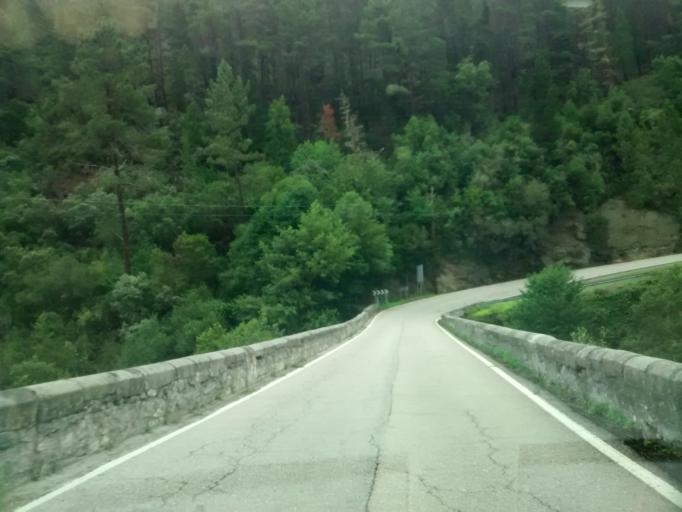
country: ES
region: Galicia
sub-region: Provincia de Ourense
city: Manzaneda
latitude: 42.3337
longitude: -7.2148
